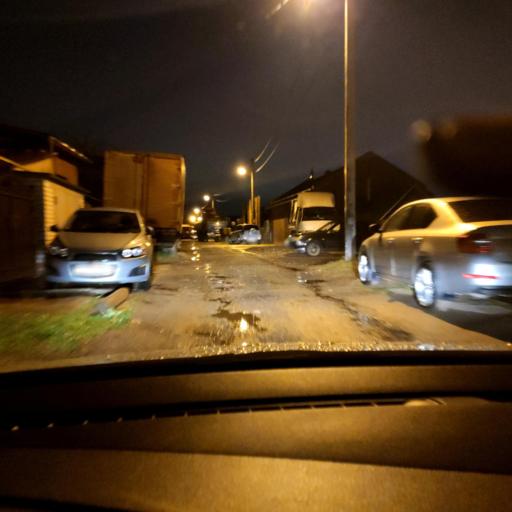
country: RU
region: Tatarstan
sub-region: Gorod Kazan'
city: Kazan
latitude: 55.8380
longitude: 49.2078
